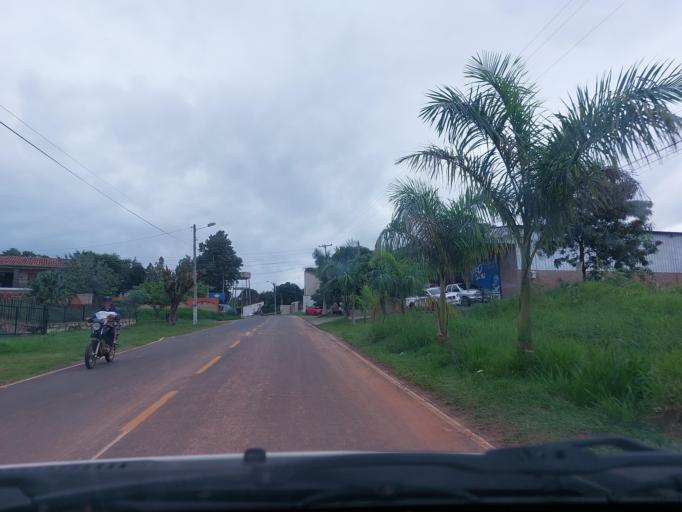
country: PY
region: San Pedro
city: Guayaybi
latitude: -24.6574
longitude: -56.4386
